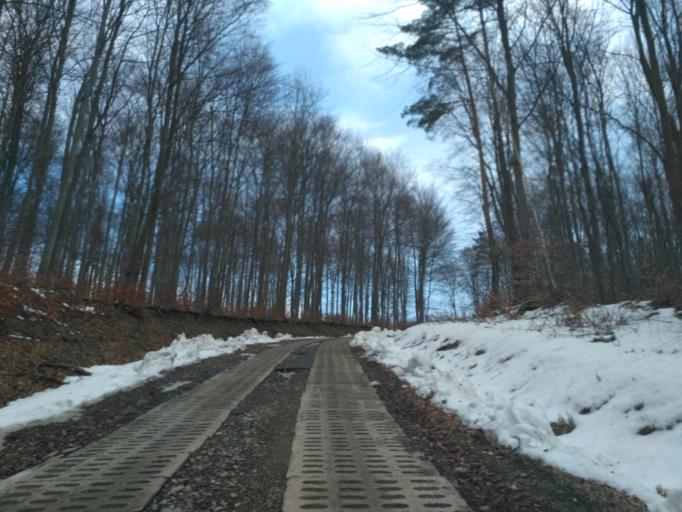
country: PL
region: Subcarpathian Voivodeship
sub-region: Powiat brzozowski
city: Dydnia
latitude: 49.6421
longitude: 22.1954
